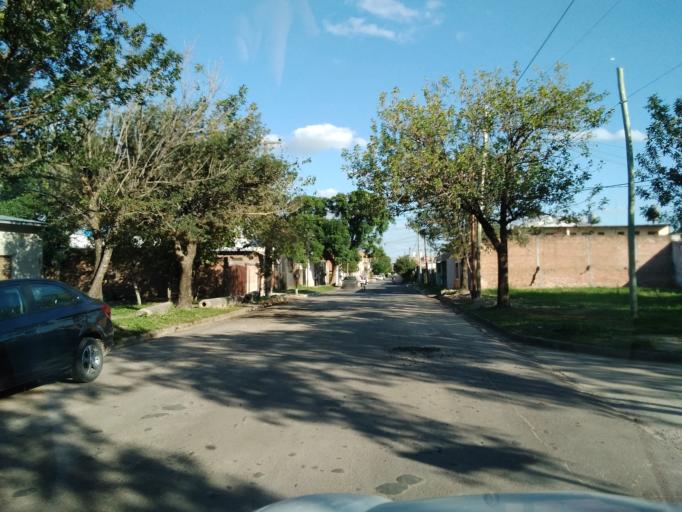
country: AR
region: Corrientes
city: Corrientes
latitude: -27.4620
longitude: -58.7825
